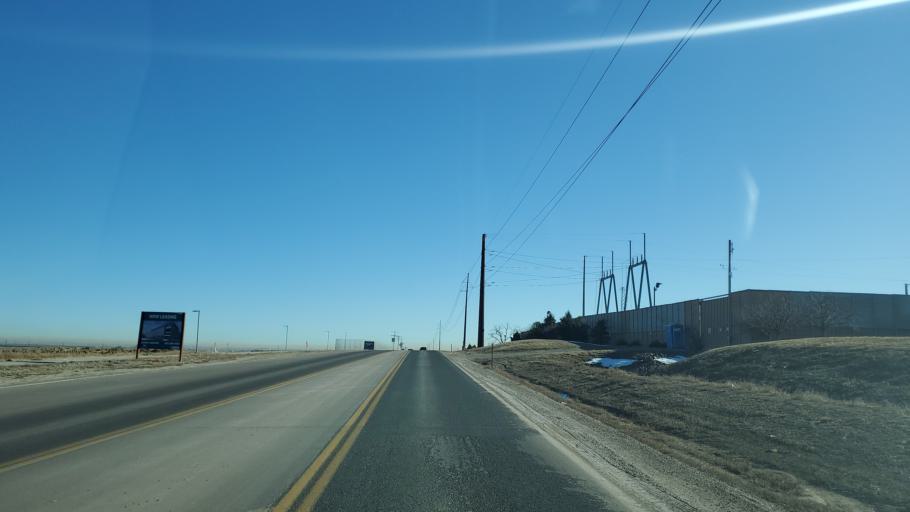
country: US
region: Colorado
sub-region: Boulder County
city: Erie
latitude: 39.9867
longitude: -105.0117
